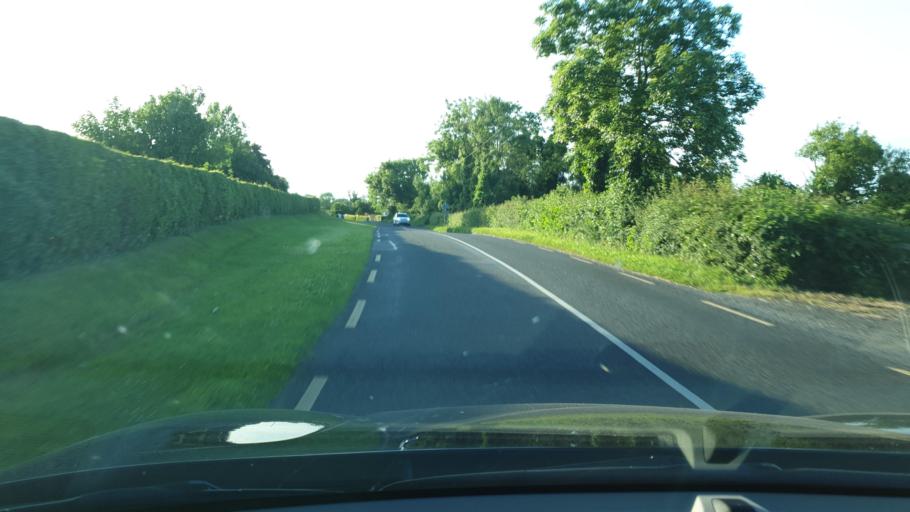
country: IE
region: Leinster
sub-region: An Mhi
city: Ratoath
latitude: 53.4995
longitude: -6.4411
